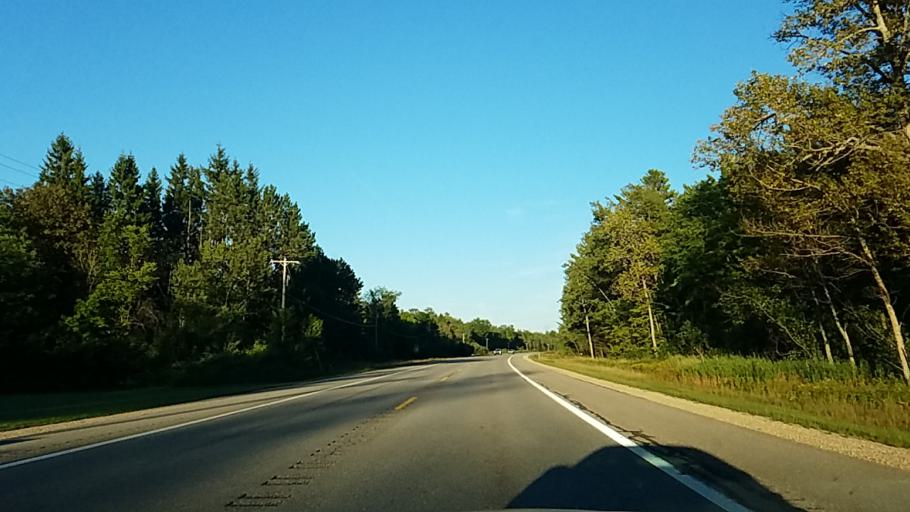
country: US
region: Michigan
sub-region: Alger County
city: Munising
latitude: 46.4423
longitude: -86.7410
